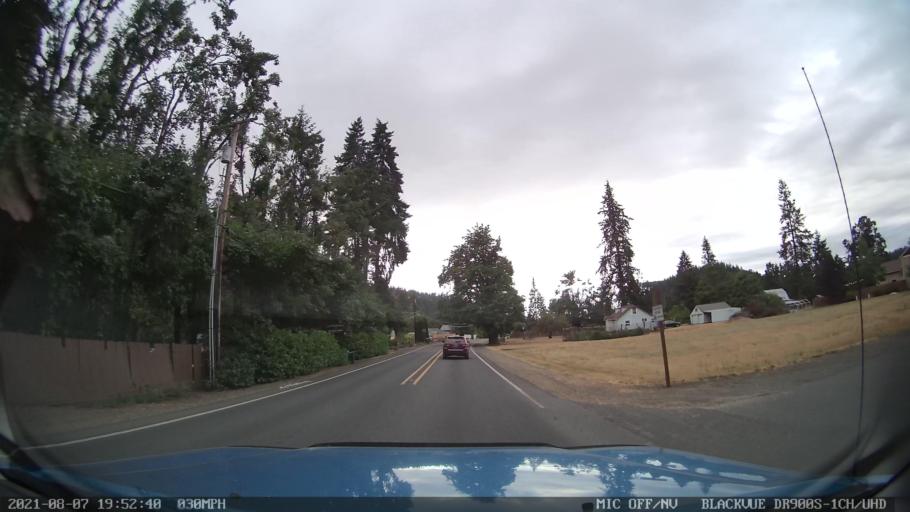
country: US
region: Oregon
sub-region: Marion County
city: Silverton
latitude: 44.9851
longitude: -122.7602
